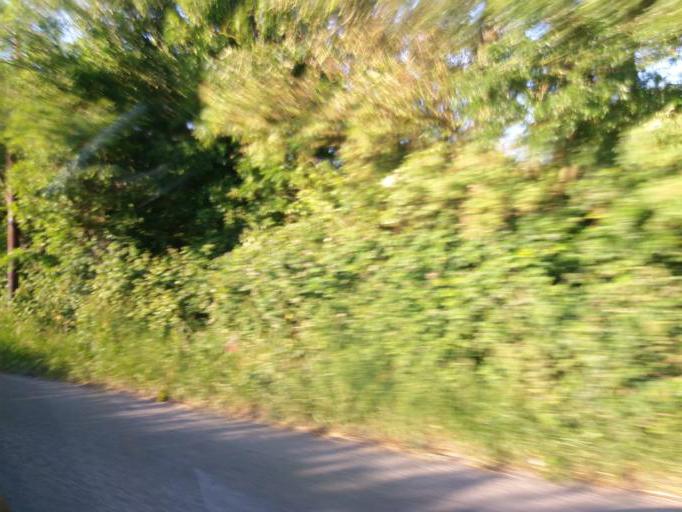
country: IE
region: Leinster
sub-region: An Mhi
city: Ashbourne
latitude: 53.5761
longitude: -6.3795
